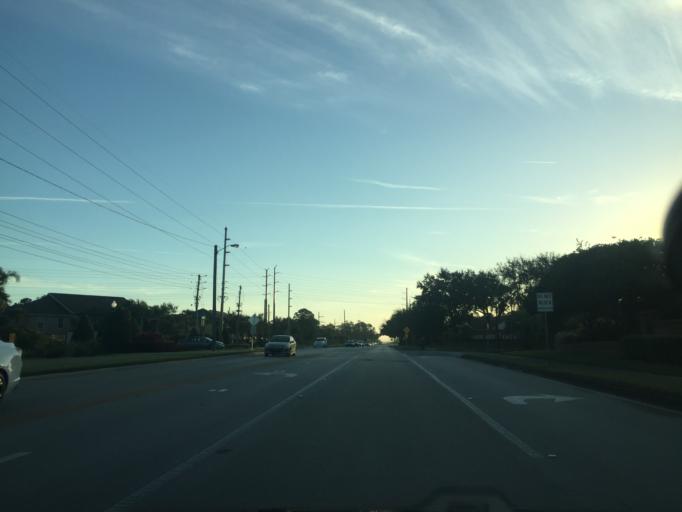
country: US
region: Florida
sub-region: Orange County
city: Alafaya
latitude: 28.6120
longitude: -81.1787
